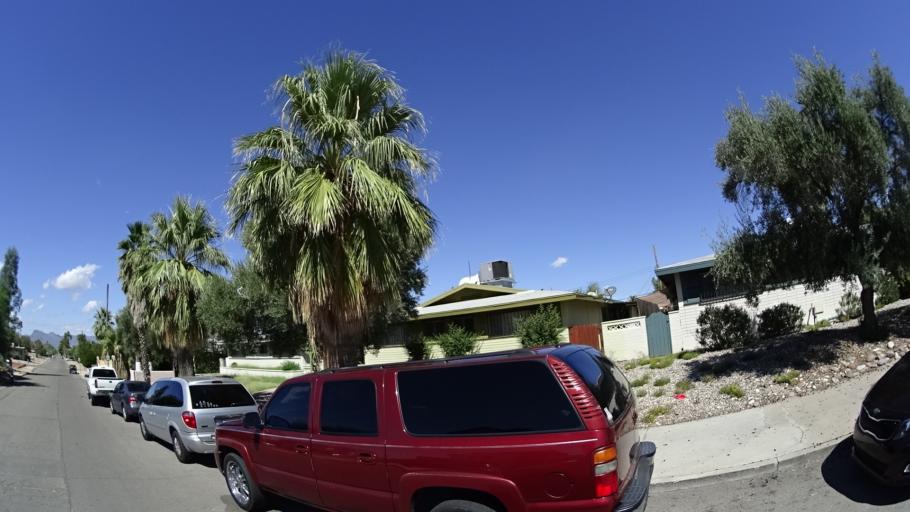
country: US
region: Arizona
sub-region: Pima County
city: Tucson
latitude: 32.2396
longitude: -110.9501
